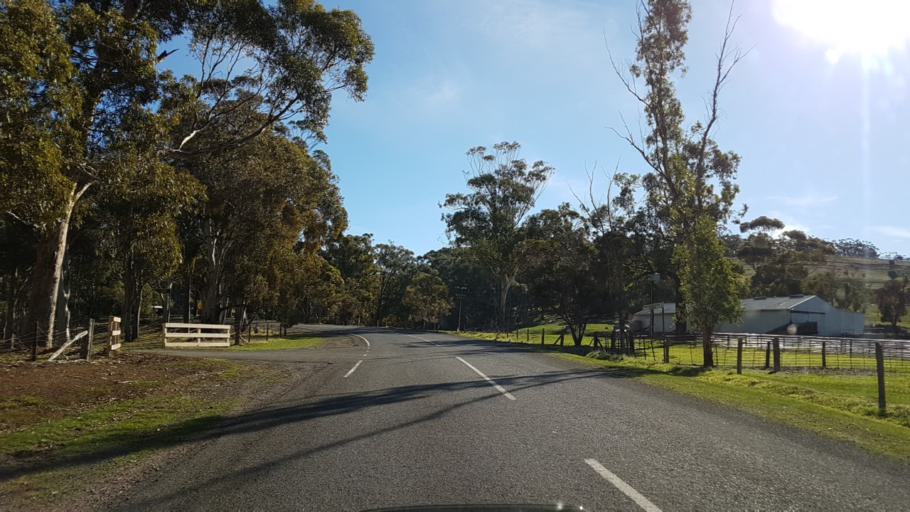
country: AU
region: South Australia
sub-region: Northern Areas
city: Jamestown
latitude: -33.2774
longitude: 138.5721
